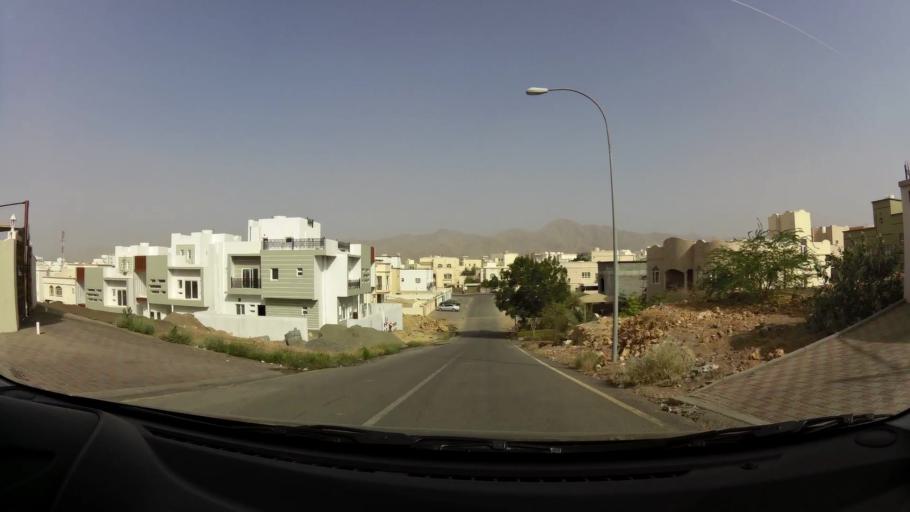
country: OM
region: Muhafazat Masqat
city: Bawshar
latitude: 23.5529
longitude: 58.3481
